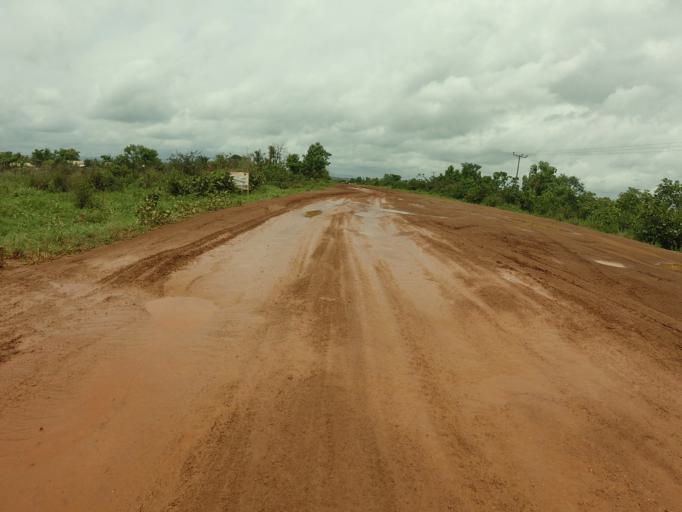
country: GH
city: Kpandae
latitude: 8.4058
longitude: 0.3984
